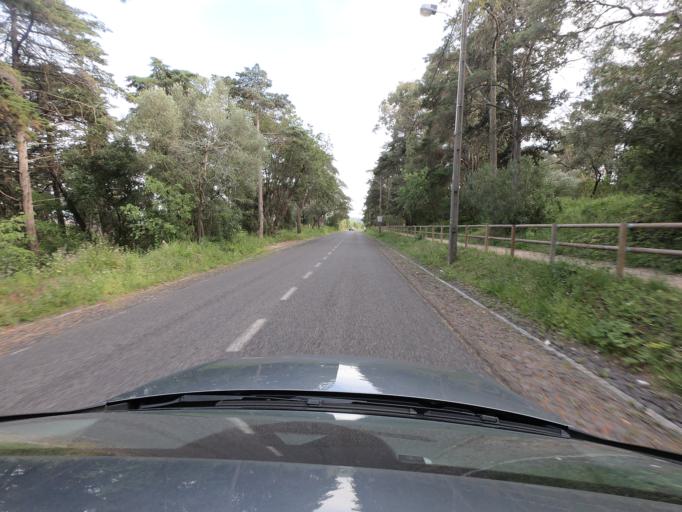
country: PT
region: Setubal
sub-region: Almada
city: Pragal
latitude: 38.7163
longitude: -9.1798
